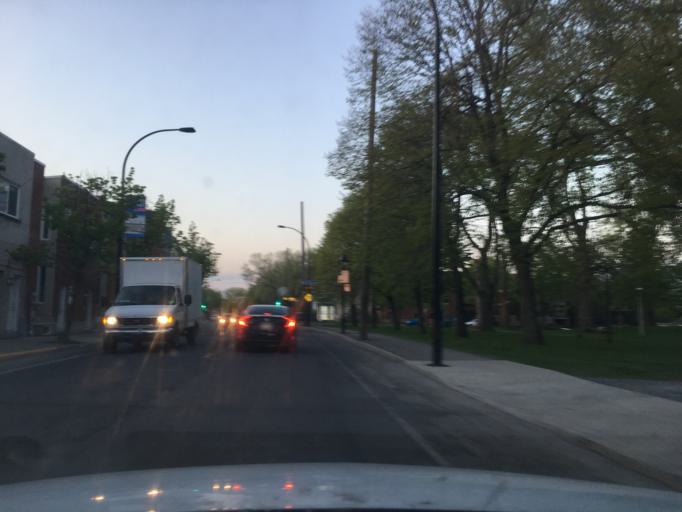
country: CA
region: Quebec
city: Westmount
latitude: 45.4756
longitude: -73.5605
